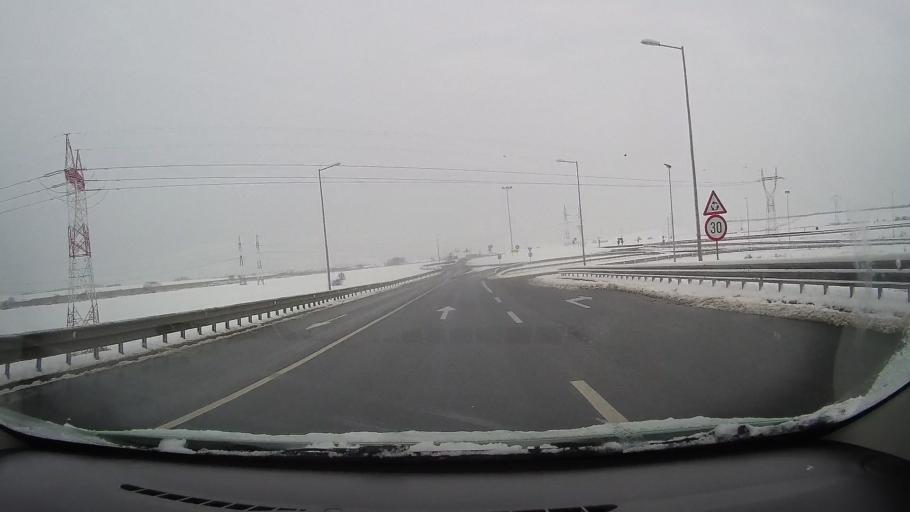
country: RO
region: Alba
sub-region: Municipiul Sebes
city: Lancram
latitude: 45.9781
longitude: 23.5208
